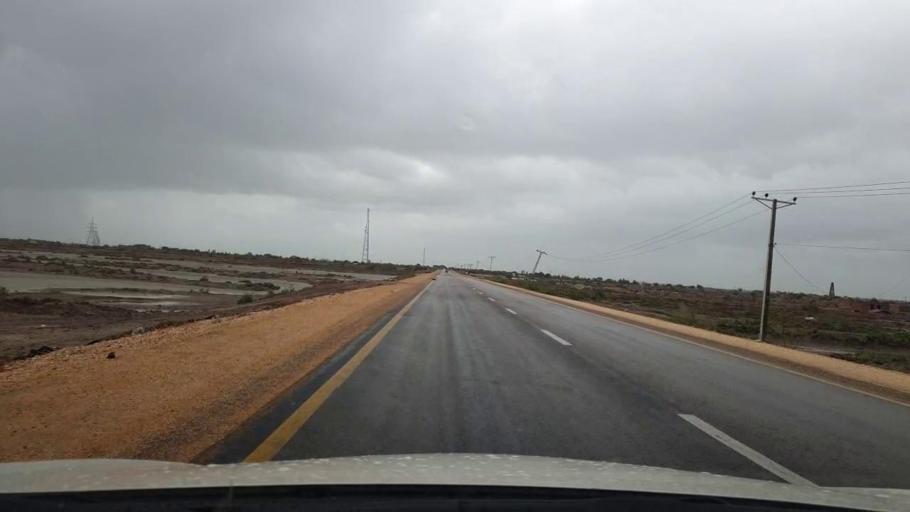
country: PK
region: Sindh
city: Kario
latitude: 24.6525
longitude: 68.6469
